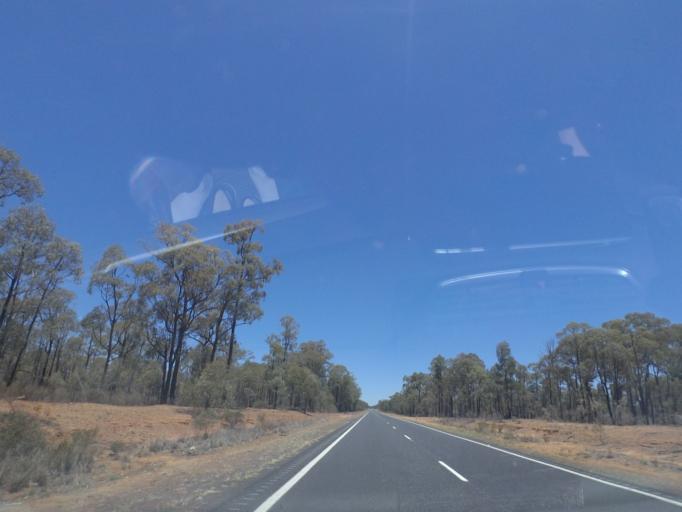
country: AU
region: New South Wales
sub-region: Warrumbungle Shire
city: Coonabarabran
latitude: -30.8638
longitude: 149.4530
